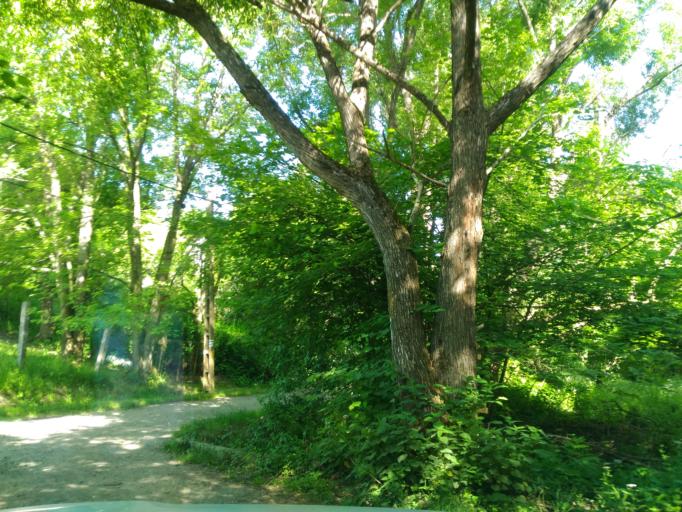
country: HU
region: Baranya
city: Hosszuheteny
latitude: 46.2101
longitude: 18.3708
